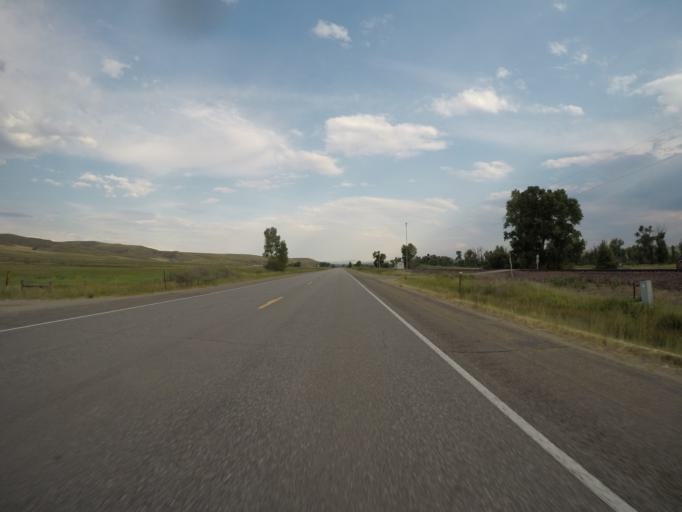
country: US
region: Colorado
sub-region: Routt County
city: Hayden
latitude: 40.5197
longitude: -107.3983
